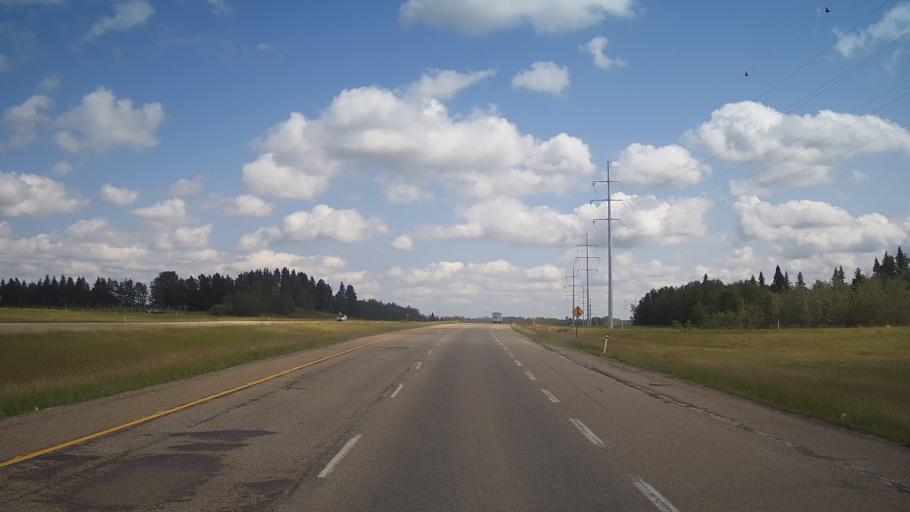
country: CA
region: Alberta
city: Sherwood Park
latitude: 53.4466
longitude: -113.2447
